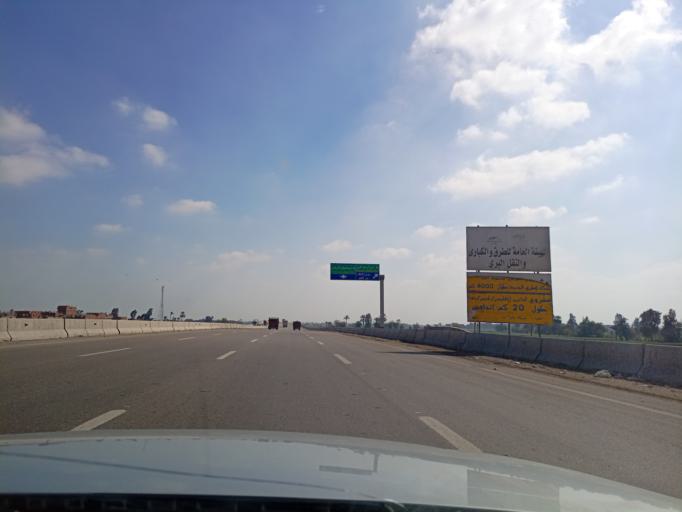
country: EG
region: Eastern Province
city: Mashtul as Suq
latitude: 30.4583
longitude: 31.3909
